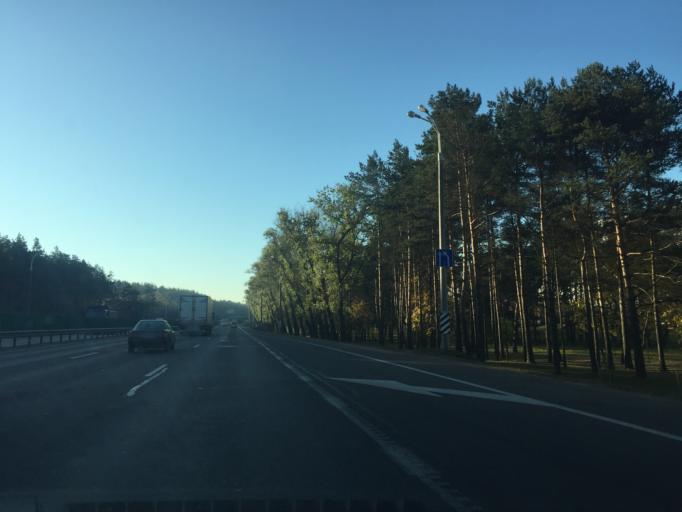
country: BY
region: Minsk
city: Vyaliki Trastsyanets
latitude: 53.8882
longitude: 27.6945
